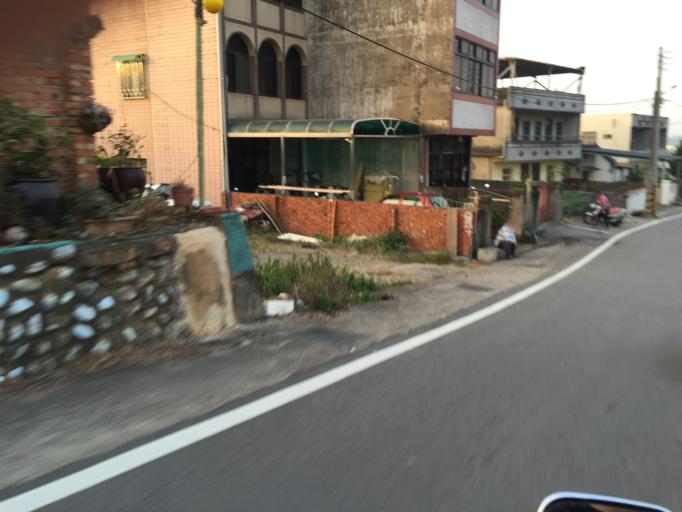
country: TW
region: Taiwan
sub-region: Miaoli
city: Miaoli
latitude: 24.4740
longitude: 120.7769
